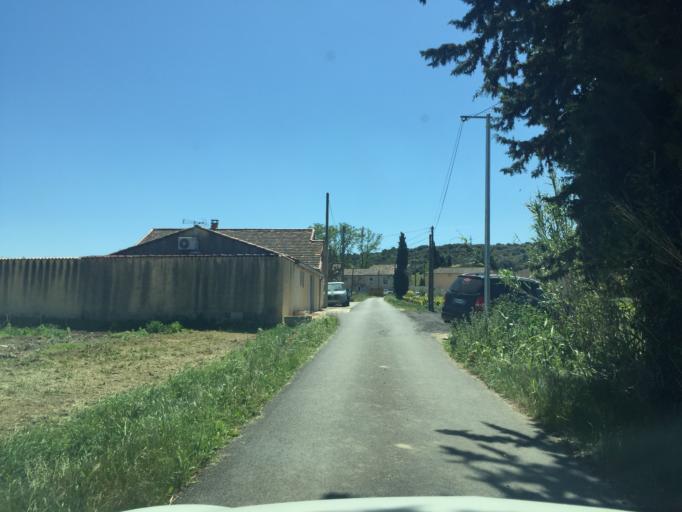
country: FR
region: Provence-Alpes-Cote d'Azur
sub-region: Departement du Vaucluse
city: Caderousse
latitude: 44.0913
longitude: 4.7935
